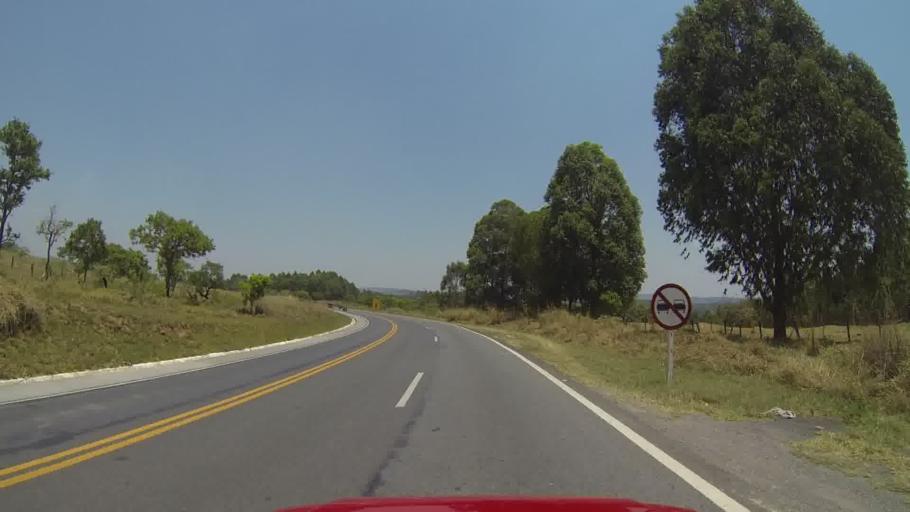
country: BR
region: Minas Gerais
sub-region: Itapecerica
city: Itapecerica
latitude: -20.3005
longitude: -45.2029
